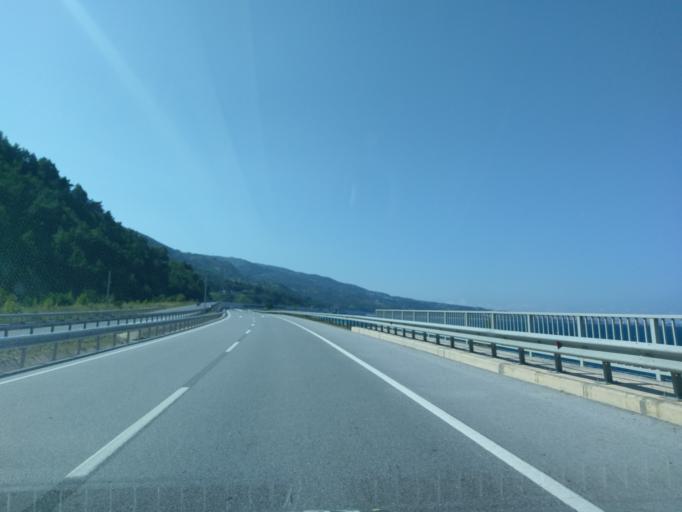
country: TR
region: Sinop
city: Gerze
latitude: 41.7523
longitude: 35.2334
